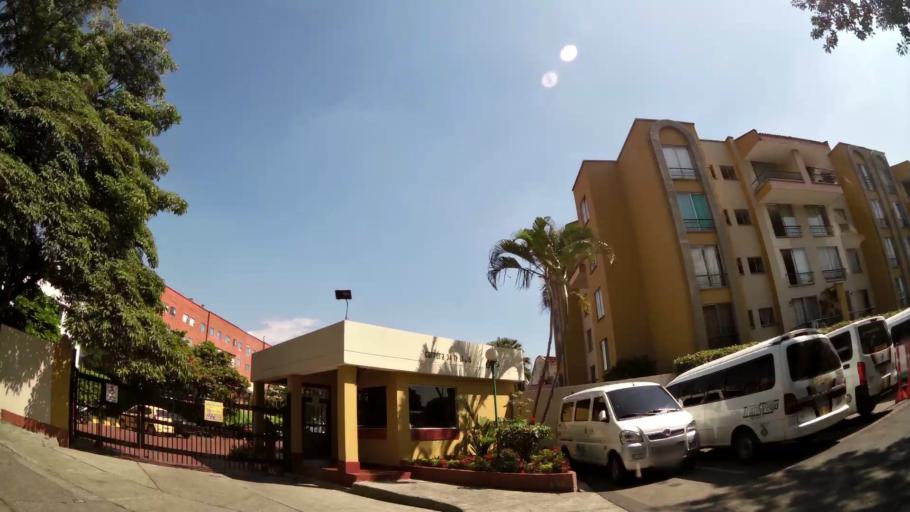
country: CO
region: Valle del Cauca
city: Cali
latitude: 3.4245
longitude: -76.5330
